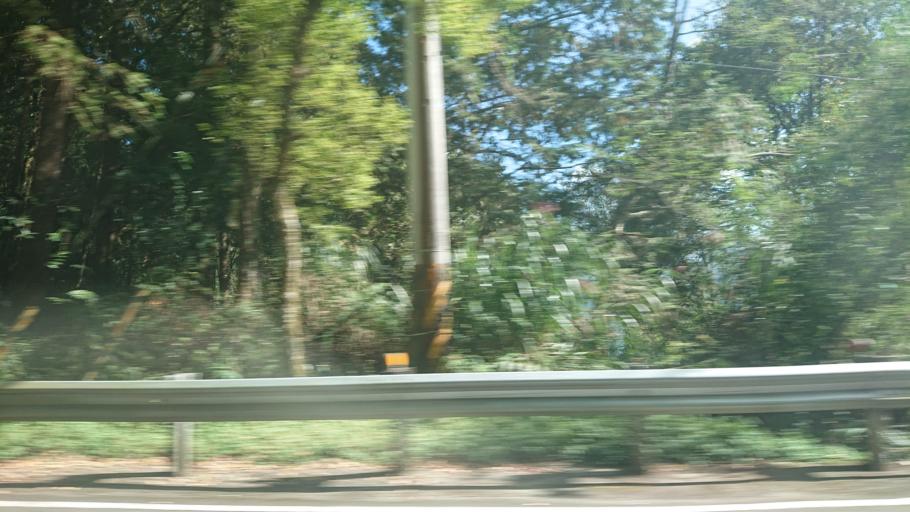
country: TW
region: Taiwan
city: Lugu
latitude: 23.5032
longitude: 120.8041
